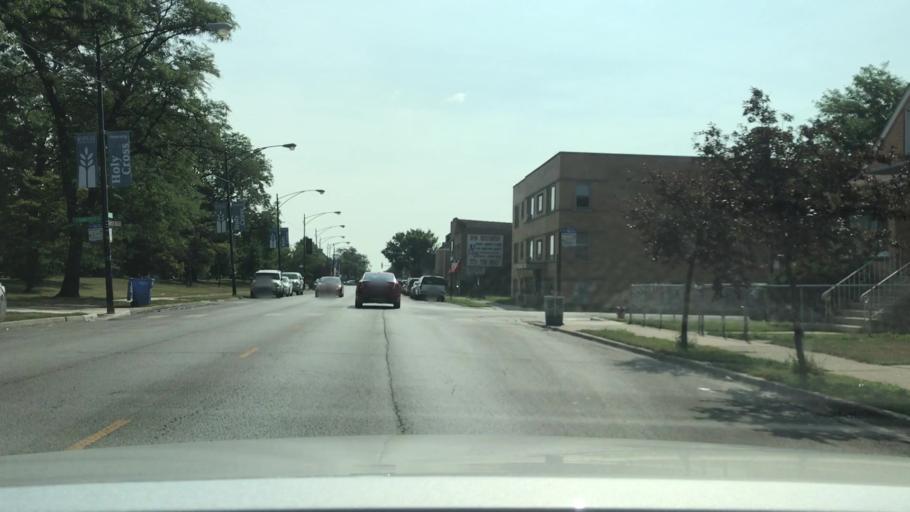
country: US
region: Illinois
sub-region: Cook County
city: Evergreen Park
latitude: 41.7645
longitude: -87.6960
